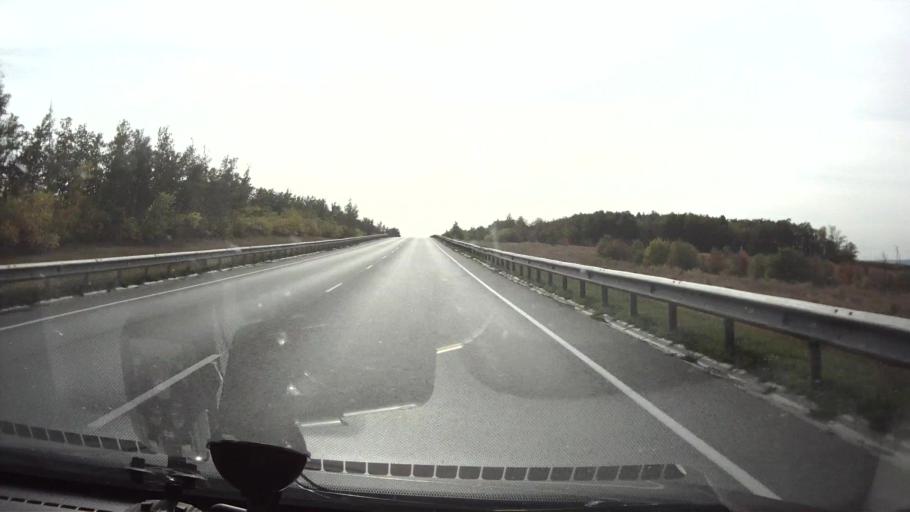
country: RU
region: Saratov
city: Balakovo
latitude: 52.1021
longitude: 47.7384
